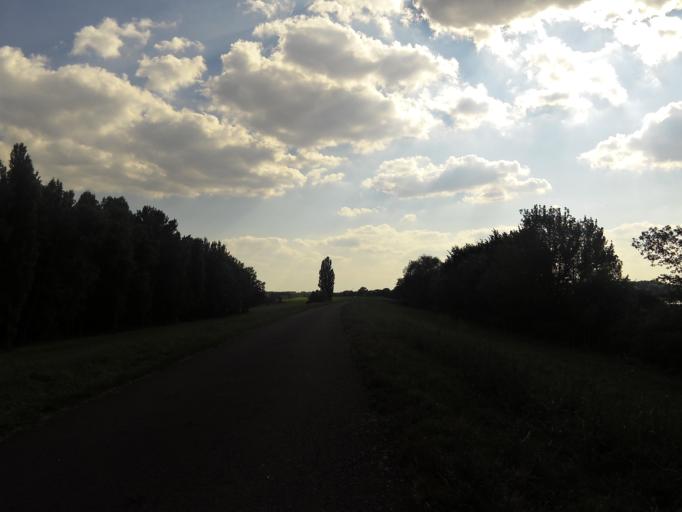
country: HU
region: Jasz-Nagykun-Szolnok
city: Abadszalok
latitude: 47.5321
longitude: 20.6170
